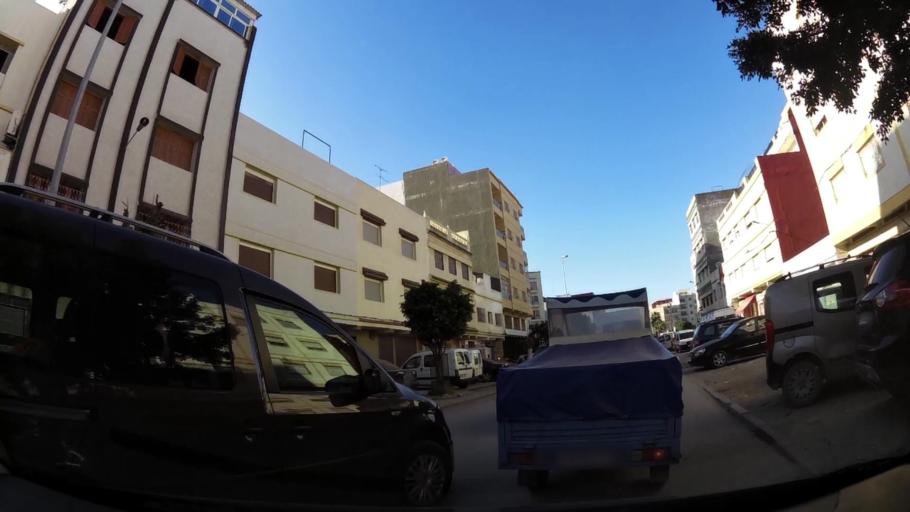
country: MA
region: Tanger-Tetouan
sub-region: Tanger-Assilah
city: Tangier
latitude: 35.7503
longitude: -5.8014
